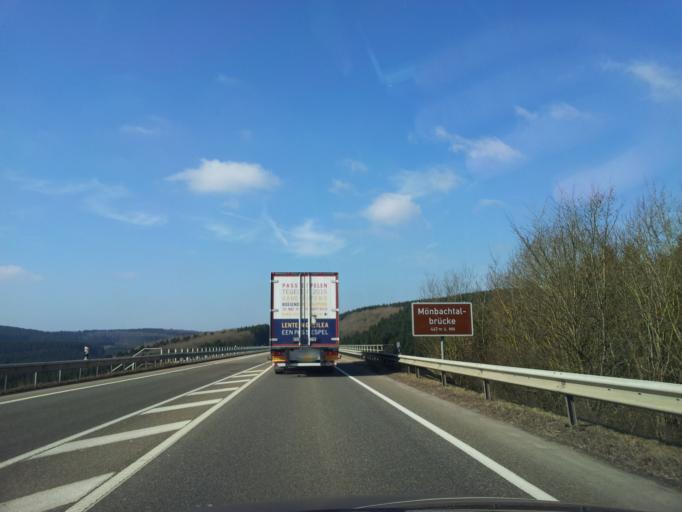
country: DE
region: Rheinland-Pfalz
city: Pittenbach
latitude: 50.2007
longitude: 6.3557
